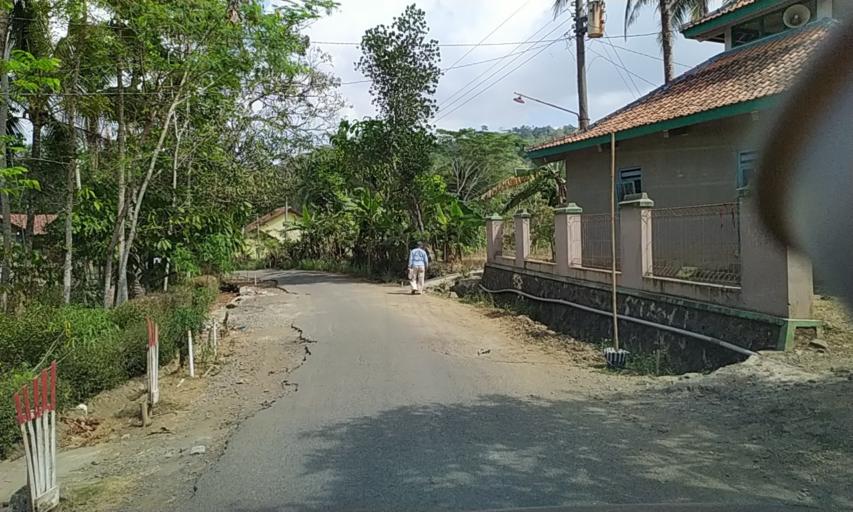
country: ID
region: Central Java
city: Prapagan
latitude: -7.5695
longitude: 109.0122
